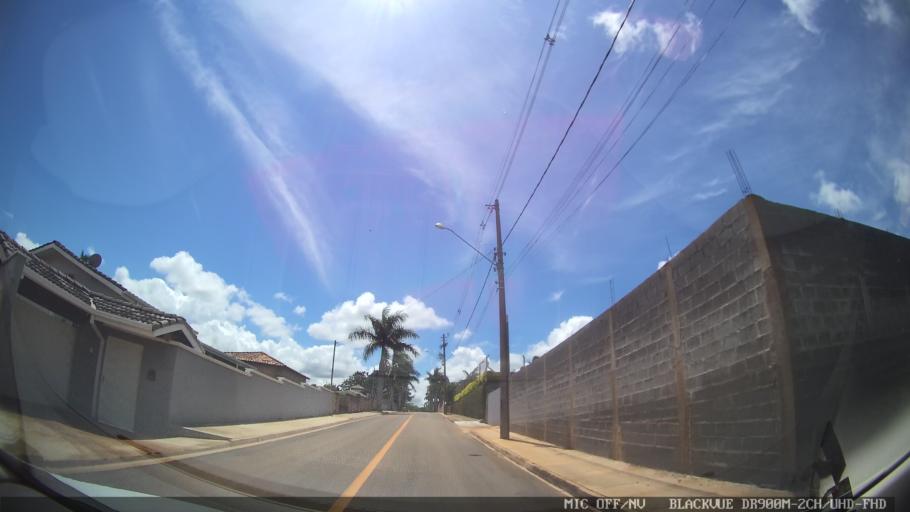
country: BR
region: Sao Paulo
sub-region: Amparo
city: Amparo
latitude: -22.8187
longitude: -46.6924
